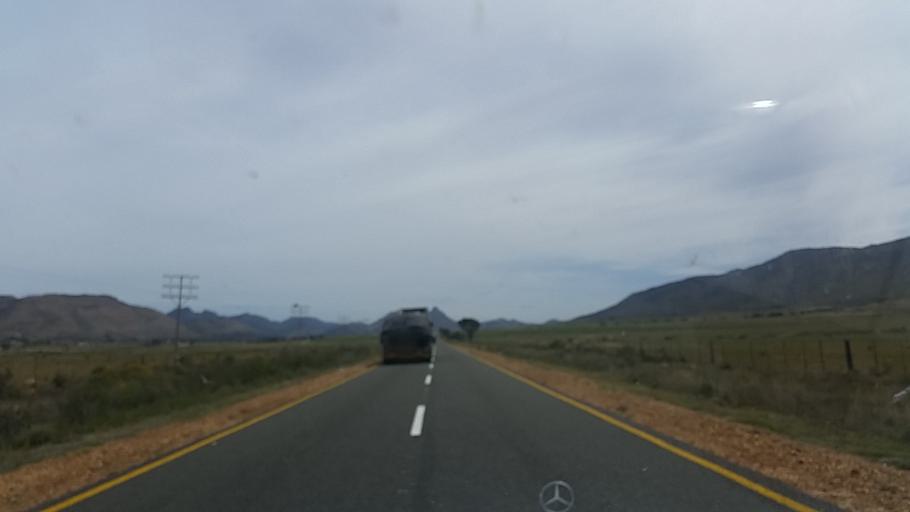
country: ZA
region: Western Cape
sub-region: Eden District Municipality
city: George
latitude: -33.8119
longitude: 22.5344
